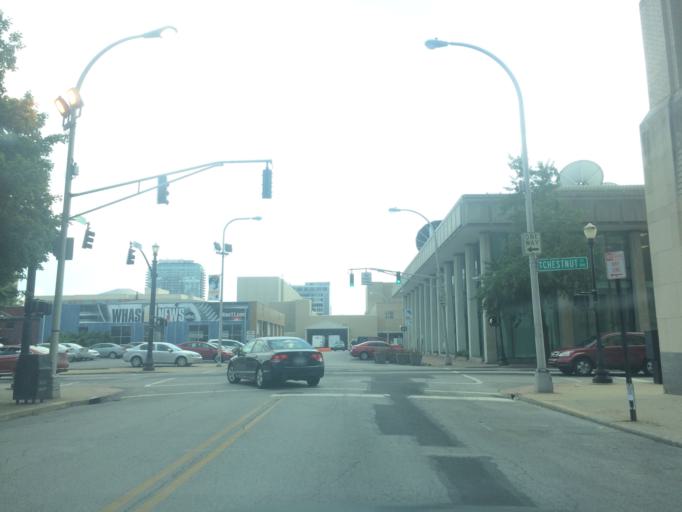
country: US
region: Kentucky
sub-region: Jefferson County
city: Louisville
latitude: 38.2494
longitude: -85.7603
